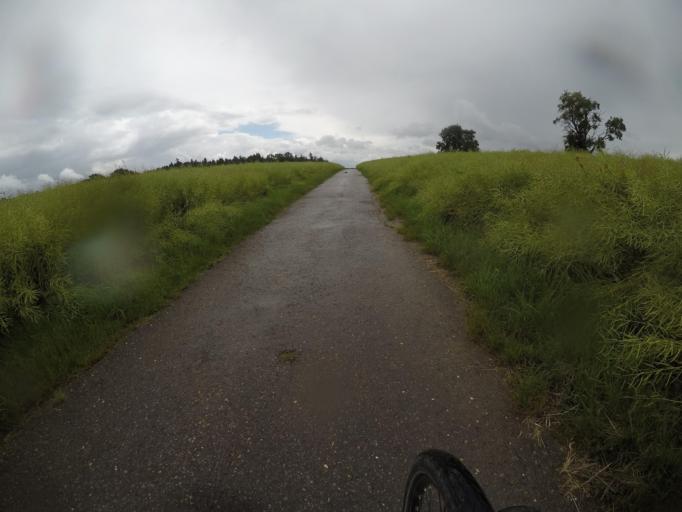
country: DE
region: Baden-Wuerttemberg
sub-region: Regierungsbezirk Stuttgart
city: Motzingen
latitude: 48.5254
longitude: 8.7856
